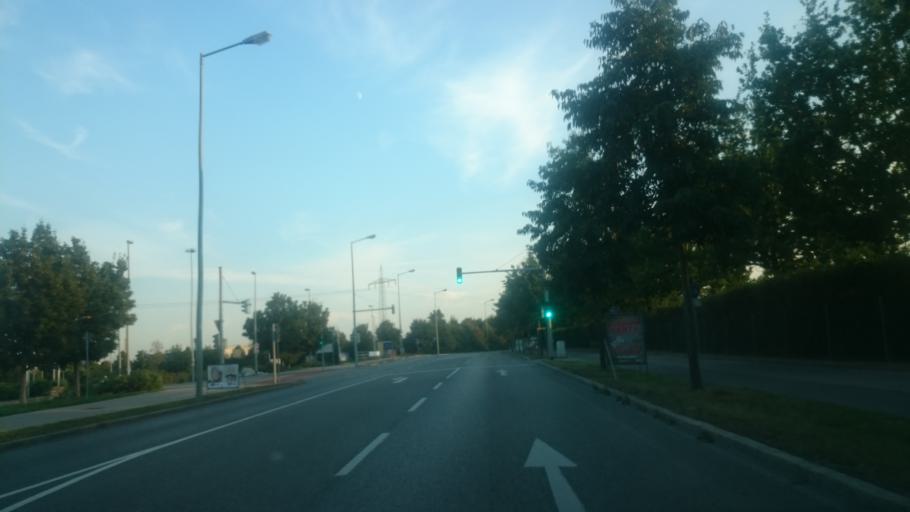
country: DE
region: Bavaria
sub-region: Swabia
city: Gersthofen
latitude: 48.4037
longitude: 10.8699
